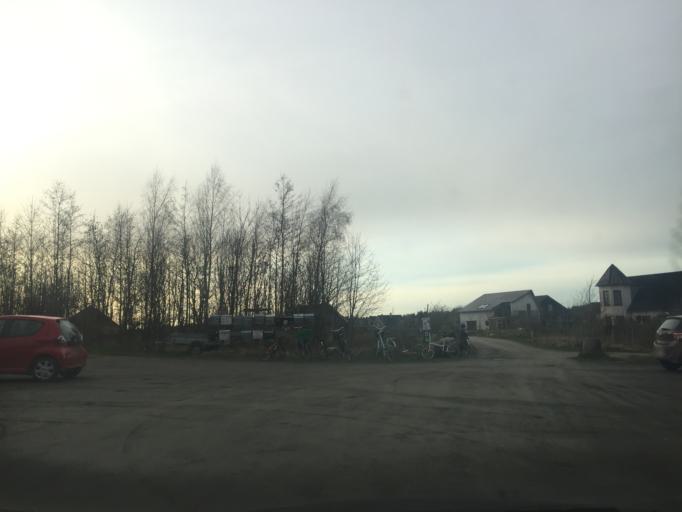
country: DK
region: Zealand
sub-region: Ringsted Kommune
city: Ringsted
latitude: 55.4940
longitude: 11.8207
